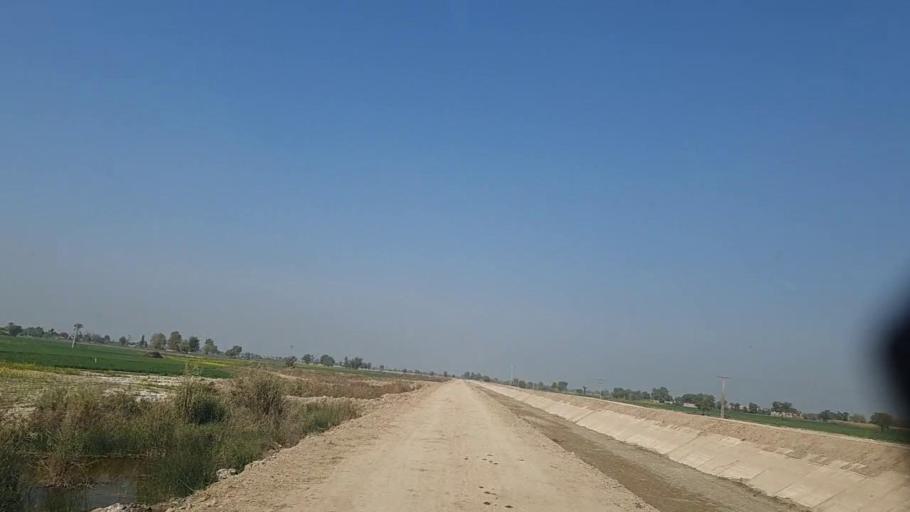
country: PK
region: Sindh
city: Sakrand
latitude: 26.1561
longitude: 68.3286
